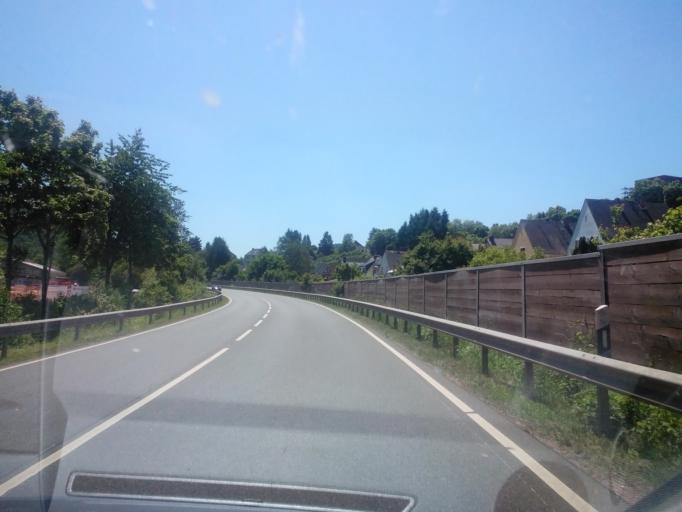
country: DE
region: Rheinland-Pfalz
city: Saarburg
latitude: 49.6034
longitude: 6.5410
